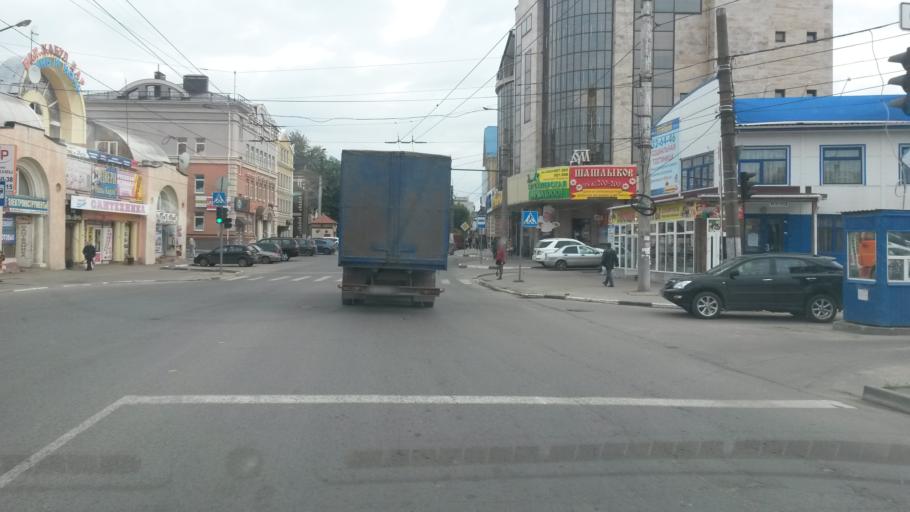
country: RU
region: Ivanovo
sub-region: Gorod Ivanovo
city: Ivanovo
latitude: 56.9937
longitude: 40.9815
